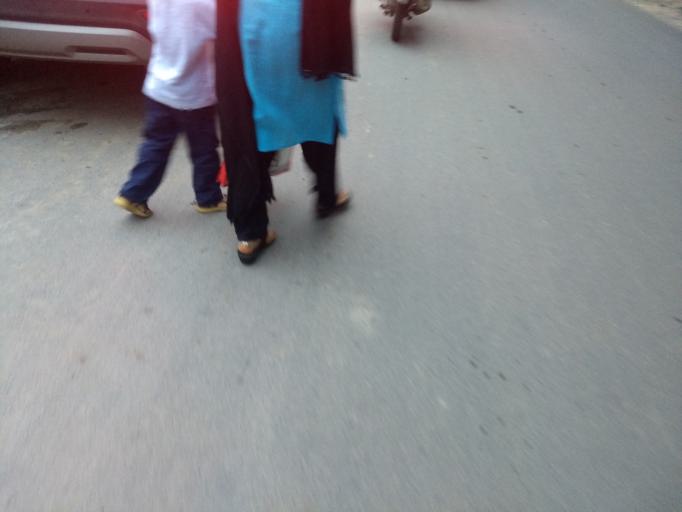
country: IN
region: Telangana
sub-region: Rangareddi
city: Kukatpalli
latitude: 17.4858
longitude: 78.3874
